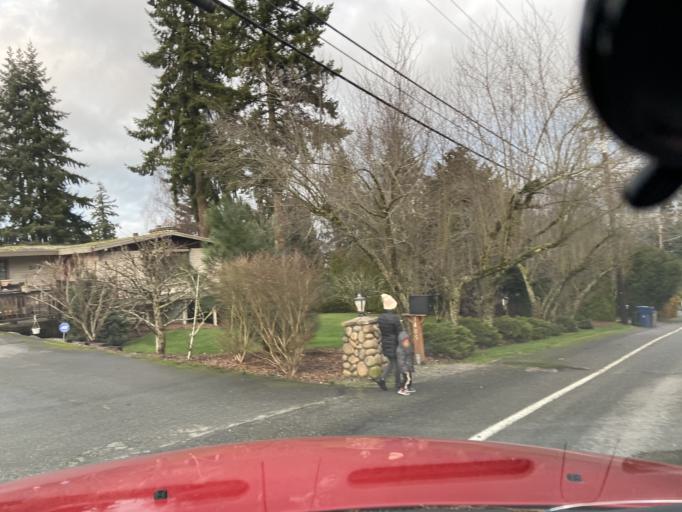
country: US
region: Washington
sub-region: Snohomish County
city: Alderwood Manor
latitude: 47.8429
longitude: -122.2793
